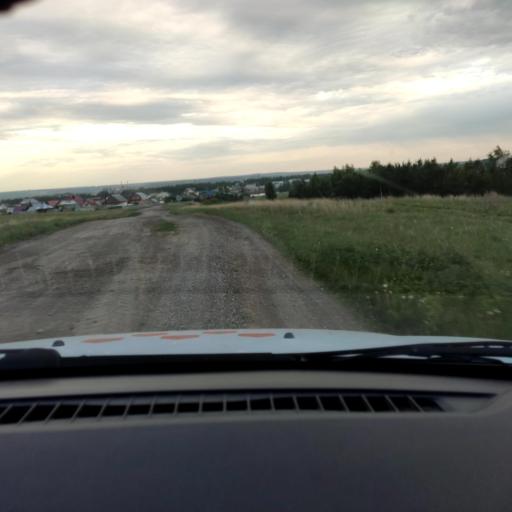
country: RU
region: Bashkortostan
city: Chishmy
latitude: 54.6110
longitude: 55.3949
